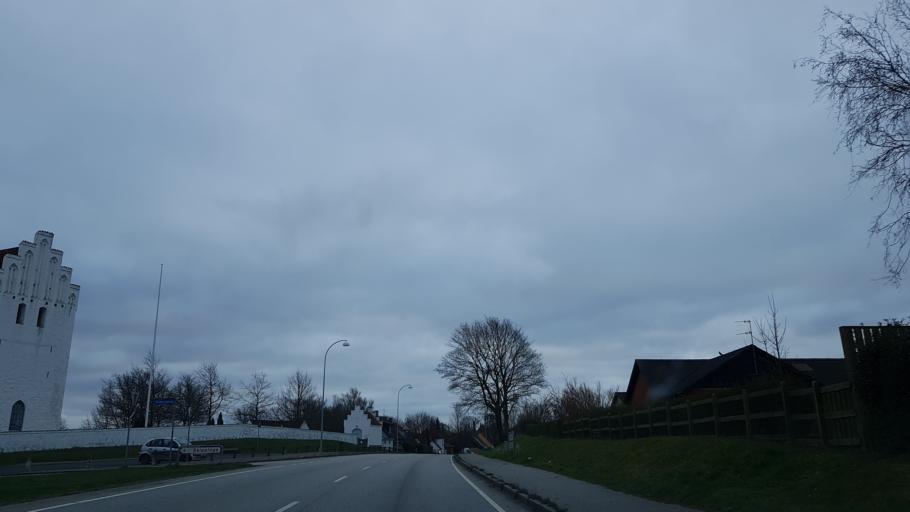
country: DK
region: Zealand
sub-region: Holbaek Kommune
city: Jyderup
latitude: 55.7172
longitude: 11.3823
